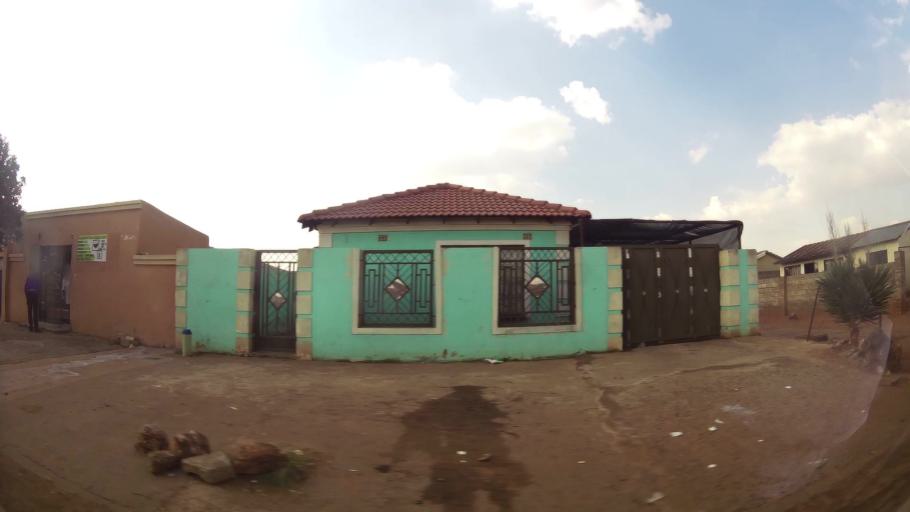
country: ZA
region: Gauteng
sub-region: Ekurhuleni Metropolitan Municipality
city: Germiston
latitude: -26.3193
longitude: 28.2019
